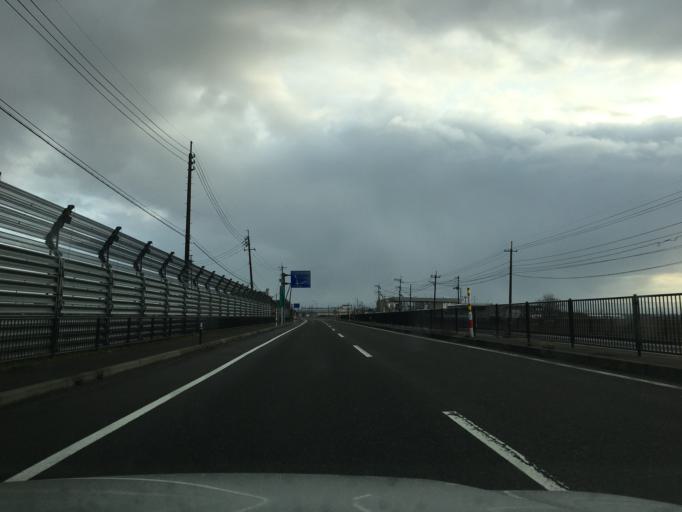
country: JP
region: Yamagata
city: Tsuruoka
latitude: 38.7224
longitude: 139.7693
